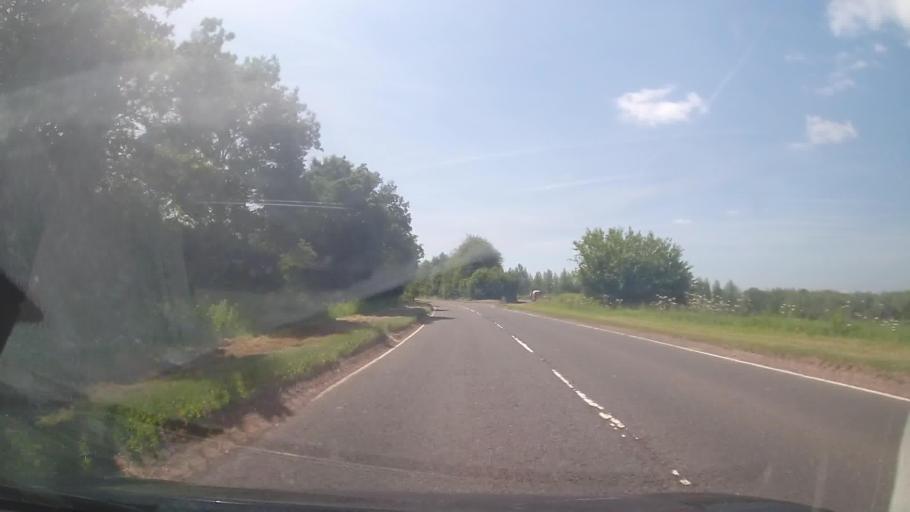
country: GB
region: England
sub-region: Herefordshire
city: Kimbolton
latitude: 52.2523
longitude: -2.7190
